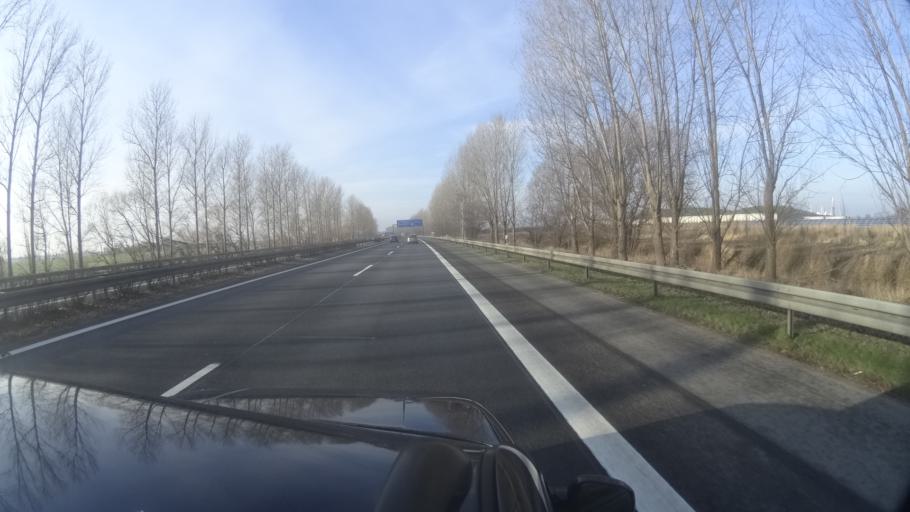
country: DE
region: Brandenburg
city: Velten
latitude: 52.7075
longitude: 13.1184
